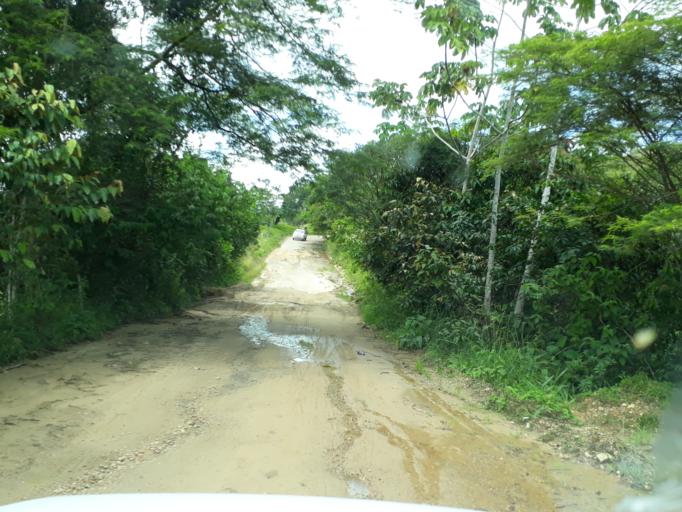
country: CO
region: Cundinamarca
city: Medina
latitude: 4.5973
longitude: -73.2966
